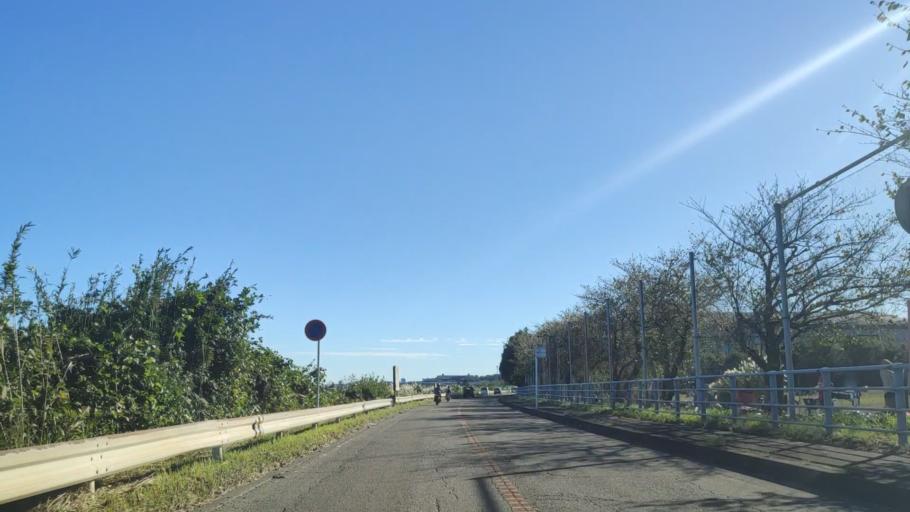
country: JP
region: Kanagawa
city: Zama
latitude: 35.5076
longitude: 139.3739
